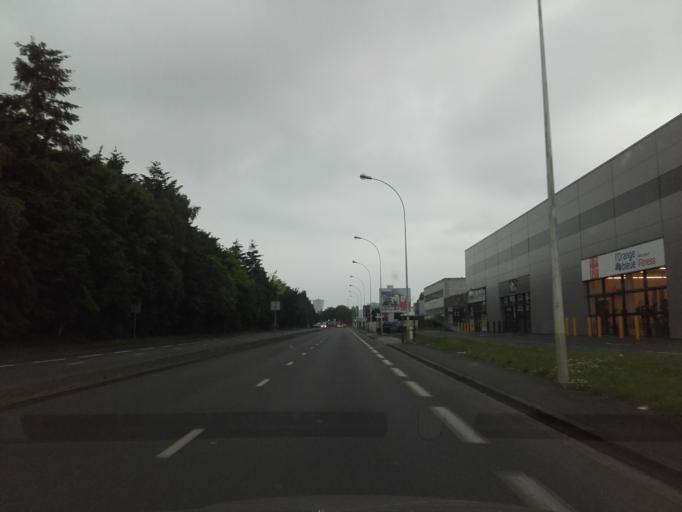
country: FR
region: Centre
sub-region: Departement d'Indre-et-Loire
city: Chanceaux-sur-Choisille
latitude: 47.4353
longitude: 0.6983
